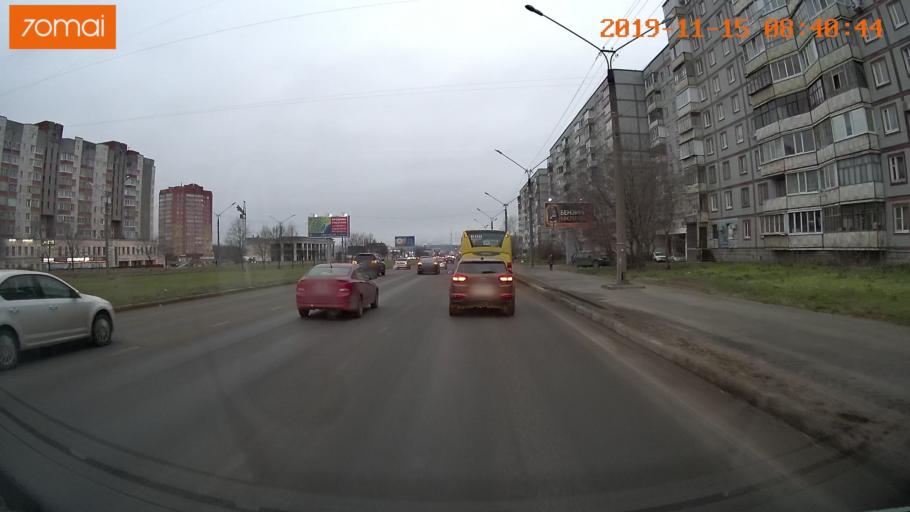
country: RU
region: Vologda
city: Cherepovets
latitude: 59.0953
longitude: 37.9136
